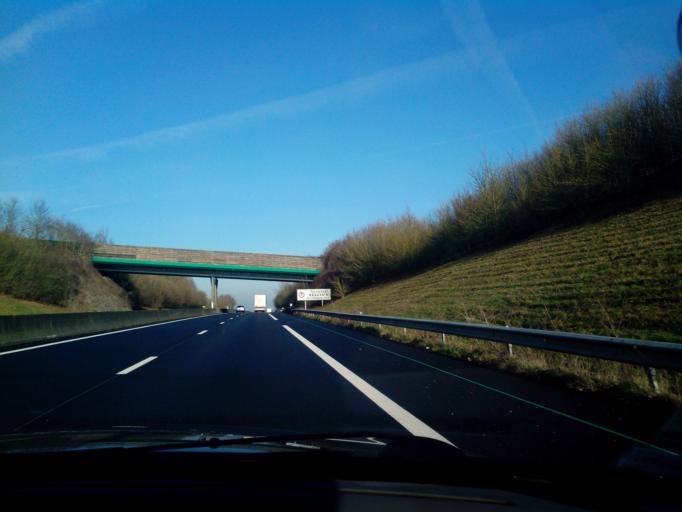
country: FR
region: Picardie
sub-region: Departement de l'Oise
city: Saint-Sulpice
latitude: 49.3736
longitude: 2.1095
